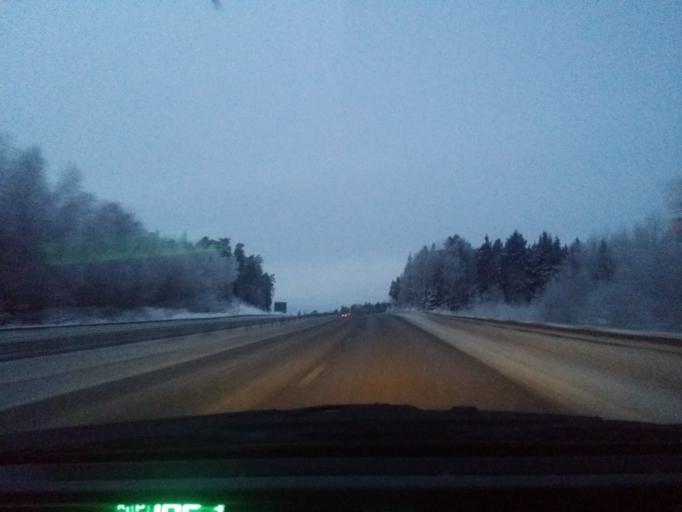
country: SE
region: Vaestmanland
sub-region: Vasteras
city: Vasteras
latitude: 59.6033
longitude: 16.4445
